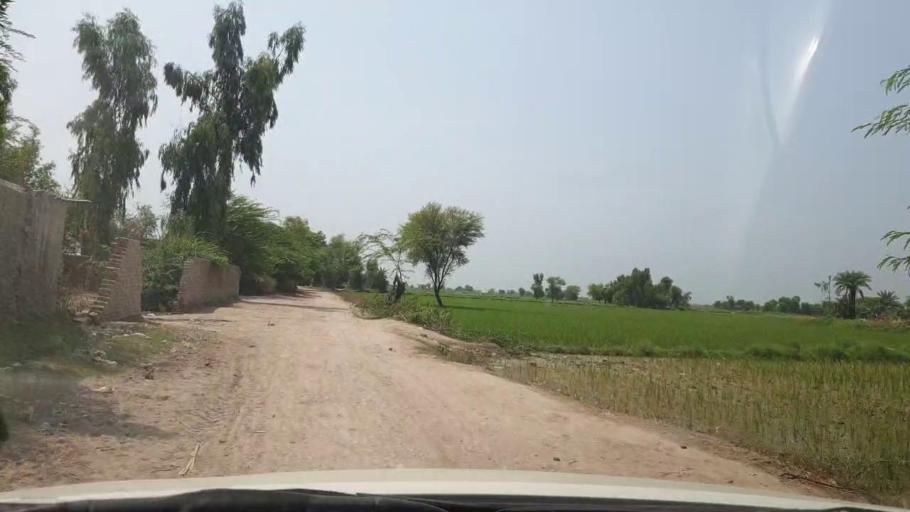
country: PK
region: Sindh
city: Rustam jo Goth
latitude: 27.9765
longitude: 68.7217
